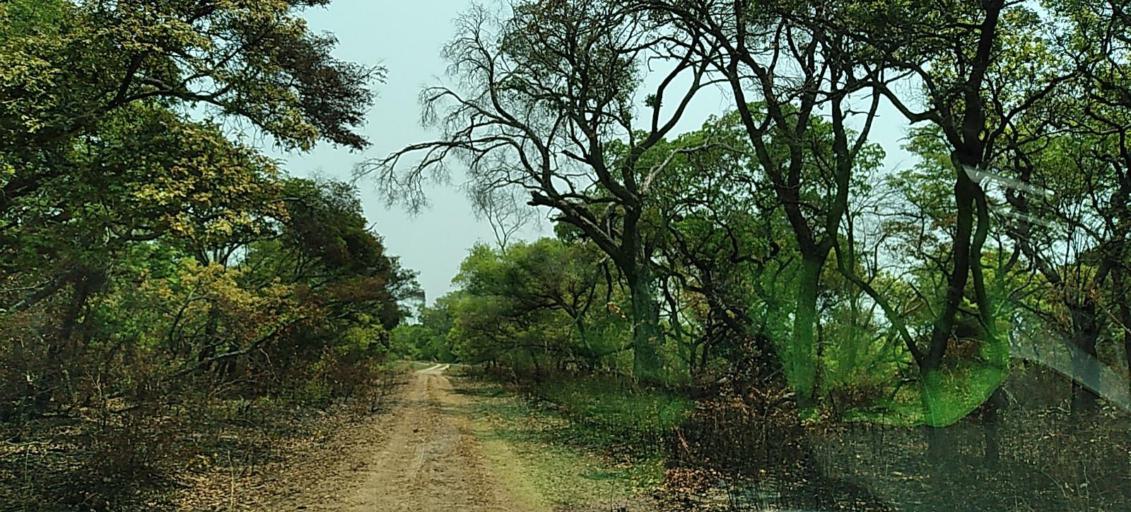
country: ZM
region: North-Western
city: Zambezi
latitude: -13.3346
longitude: 23.0177
